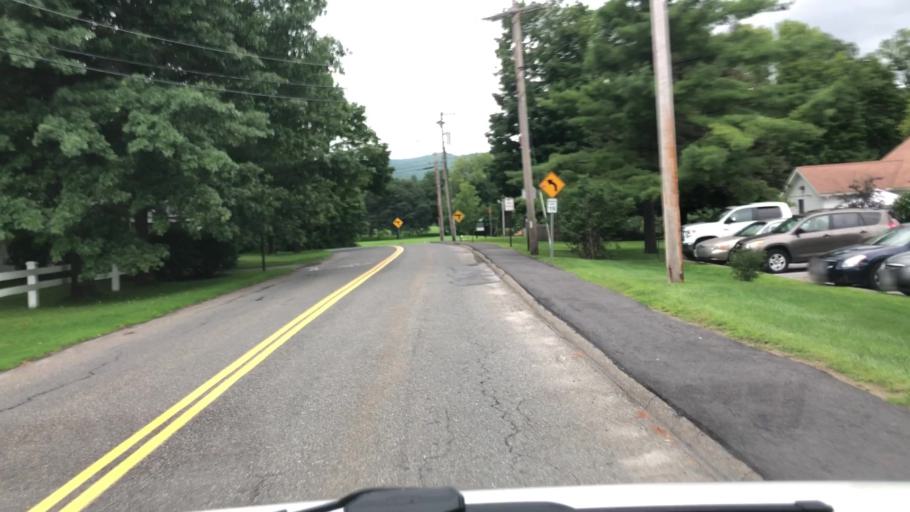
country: US
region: Massachusetts
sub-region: Berkshire County
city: Williamstown
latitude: 42.7171
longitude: -73.1977
